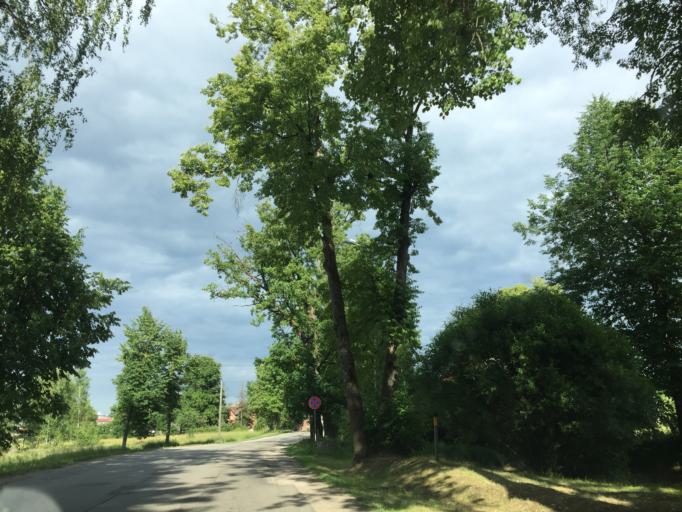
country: LV
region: Skriveri
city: Skriveri
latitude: 56.8439
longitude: 25.1505
